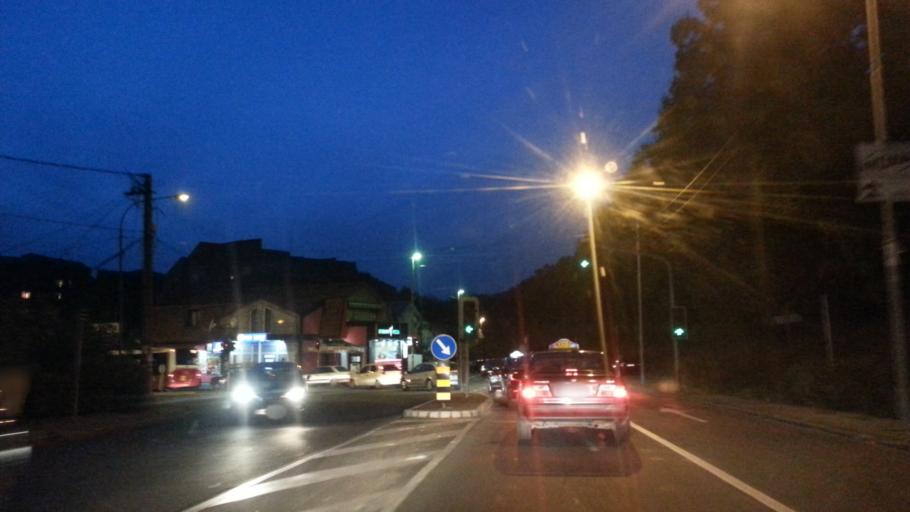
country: RS
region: Central Serbia
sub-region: Belgrade
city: Savski Venac
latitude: 44.7572
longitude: 20.4611
